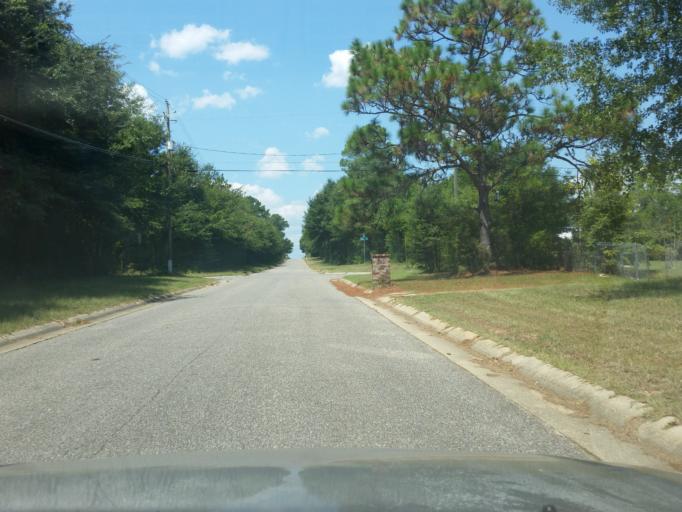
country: US
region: Florida
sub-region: Escambia County
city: Gonzalez
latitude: 30.6426
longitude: -87.2860
